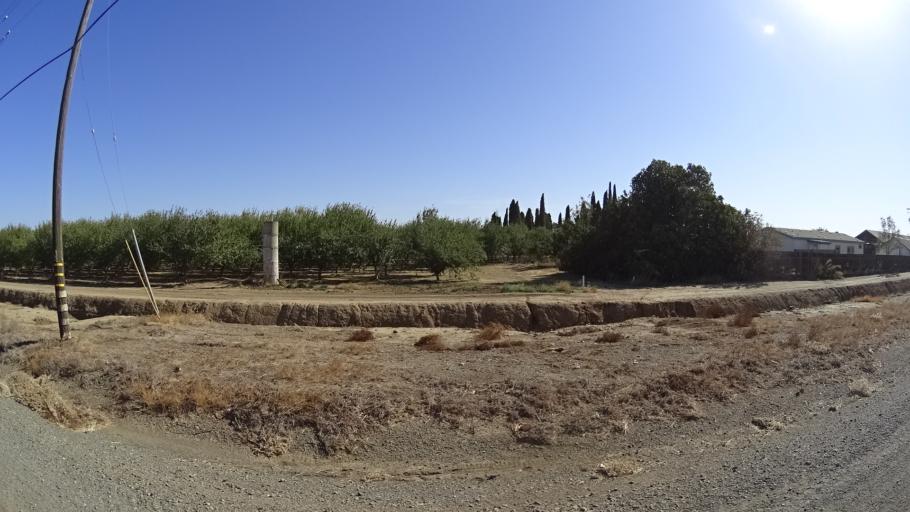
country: US
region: California
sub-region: Yolo County
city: Cottonwood
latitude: 38.6505
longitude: -121.9712
